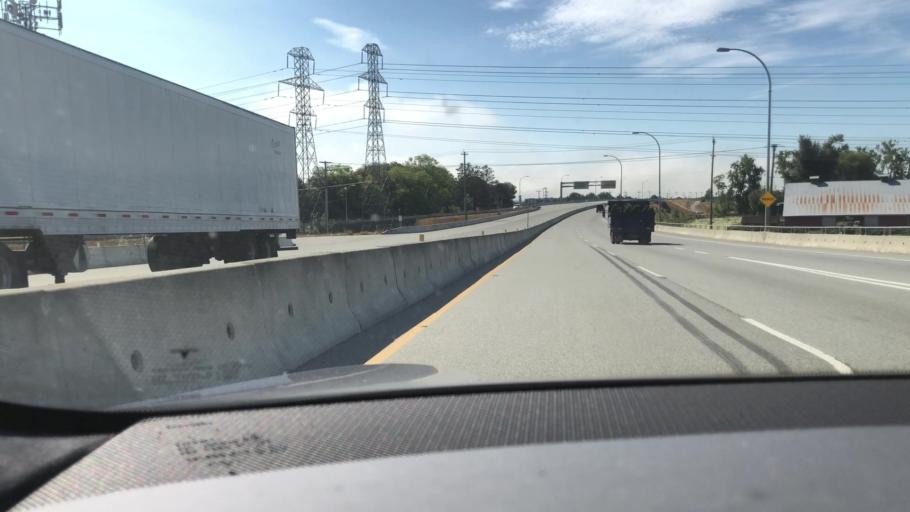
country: CA
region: British Columbia
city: Ladner
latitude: 49.0934
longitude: -123.0258
